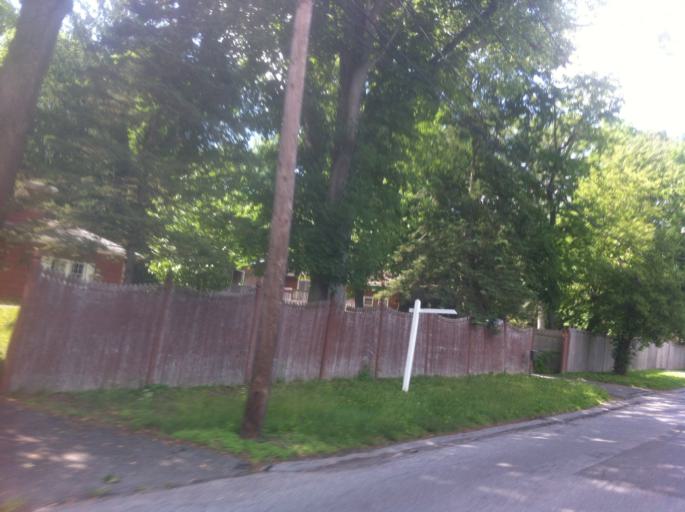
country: US
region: New York
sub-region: Nassau County
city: Glen Cove
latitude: 40.8695
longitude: -73.6177
